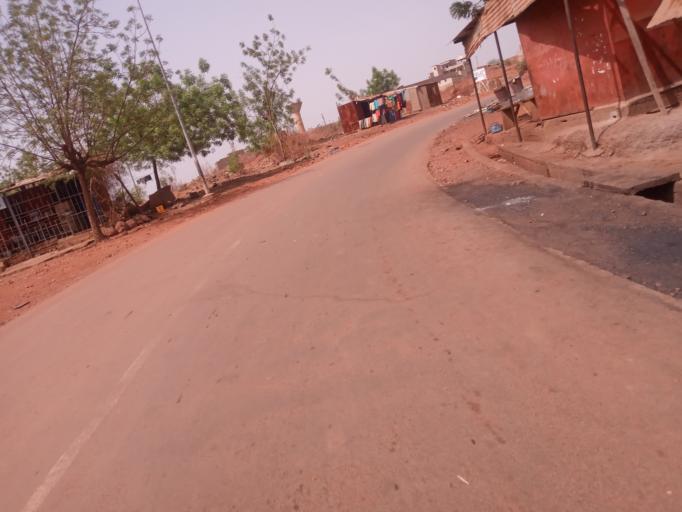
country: ML
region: Bamako
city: Bamako
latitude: 12.6164
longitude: -7.9829
